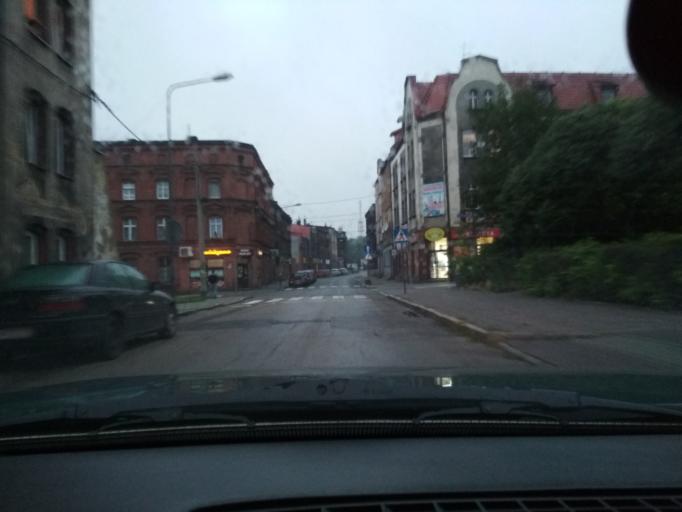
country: PL
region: Silesian Voivodeship
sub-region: Swietochlowice
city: Swietochlowice
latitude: 50.2920
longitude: 18.9204
